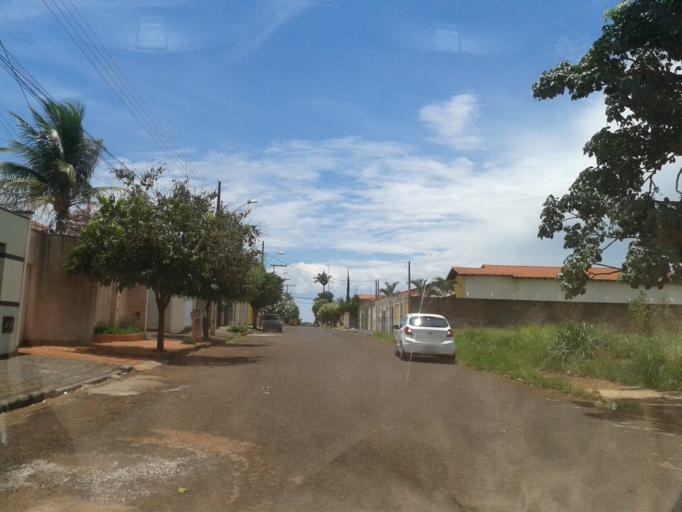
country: BR
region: Minas Gerais
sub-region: Ituiutaba
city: Ituiutaba
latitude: -18.9914
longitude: -49.4594
